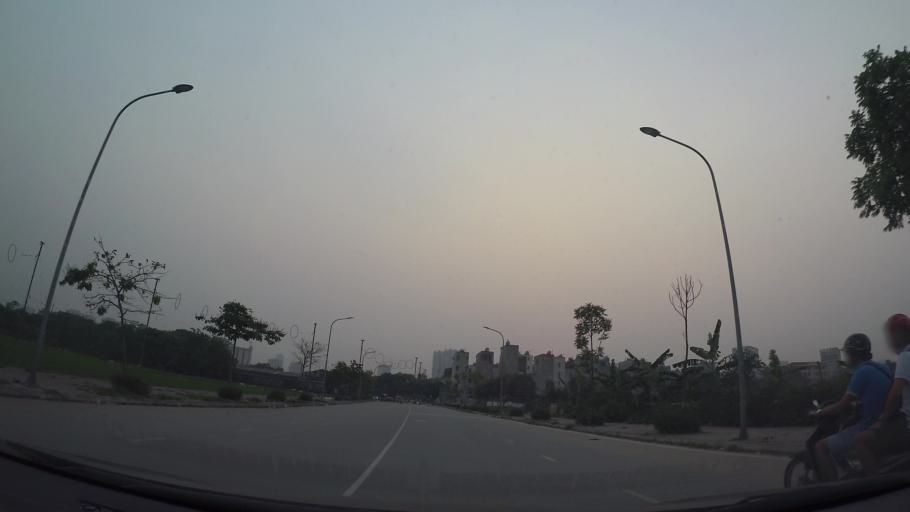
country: VN
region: Ha Noi
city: Thanh Xuan
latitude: 20.9773
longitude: 105.8001
